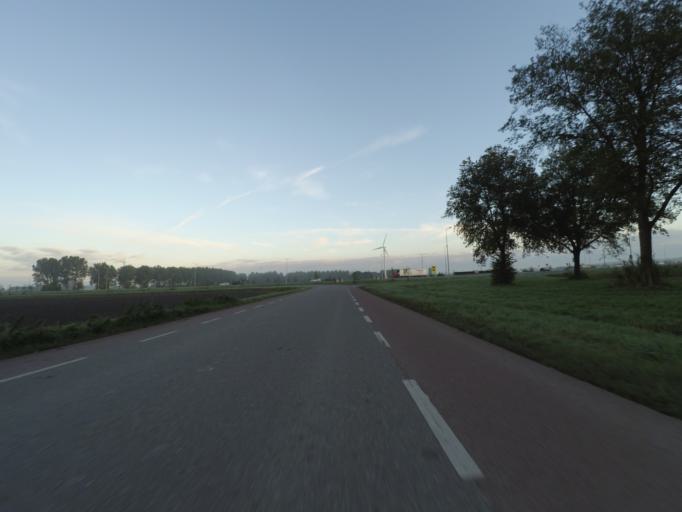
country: NL
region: Utrecht
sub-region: Gemeente Bunschoten
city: Bunschoten
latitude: 52.3216
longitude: 5.4331
